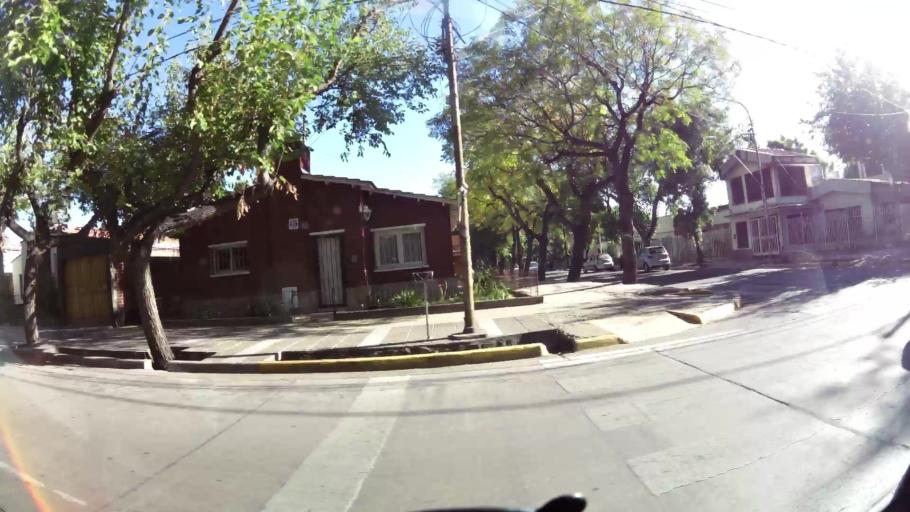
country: AR
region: Mendoza
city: Las Heras
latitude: -32.8689
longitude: -68.8517
